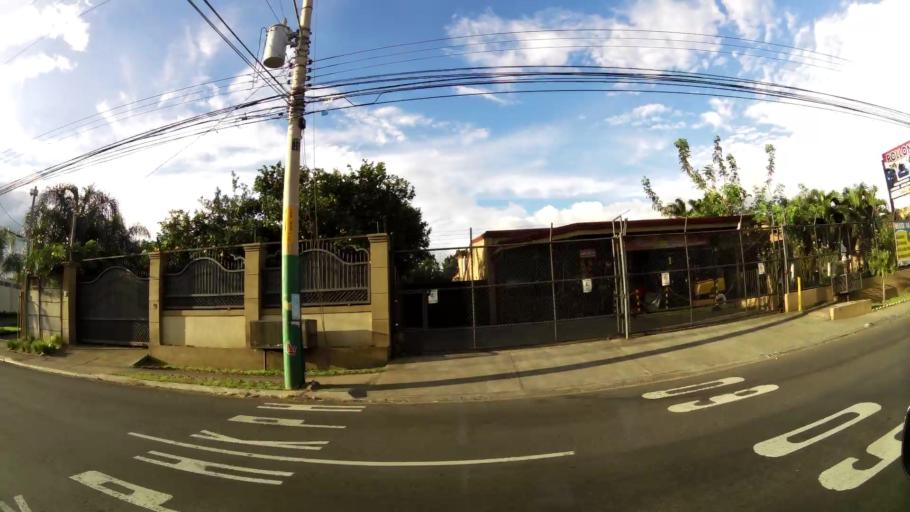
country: CR
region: Heredia
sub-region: Canton de Belen
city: San Antonio
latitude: 10.0068
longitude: -84.1777
